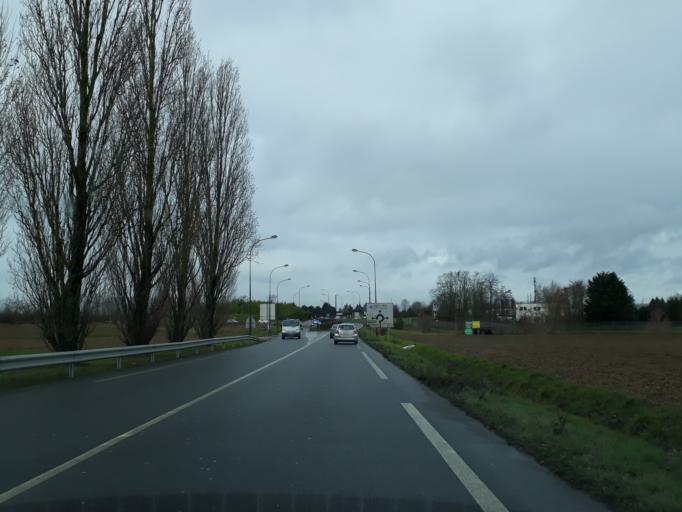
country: FR
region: Ile-de-France
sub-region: Departement de l'Essonne
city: Gometz-le-Chatel
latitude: 48.6712
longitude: 2.1403
